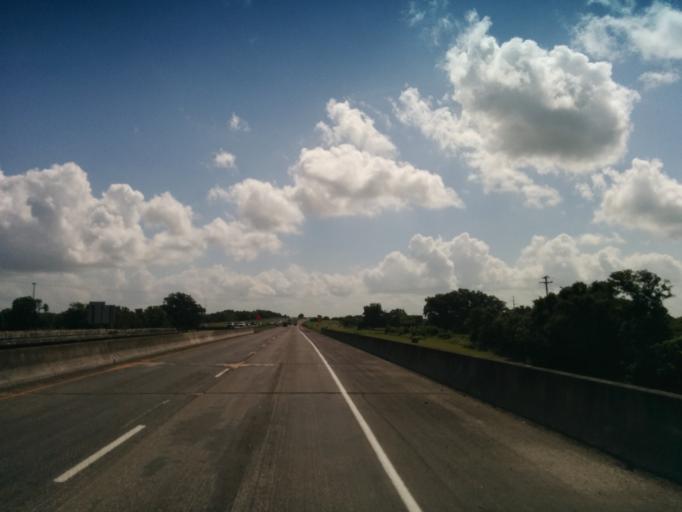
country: US
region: Texas
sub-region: Colorado County
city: Columbus
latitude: 29.7000
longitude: -96.5251
